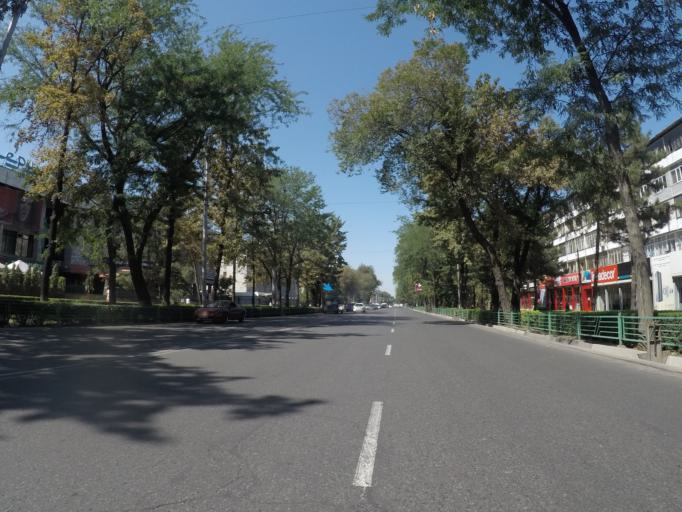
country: KG
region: Chuy
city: Bishkek
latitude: 42.8765
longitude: 74.5913
